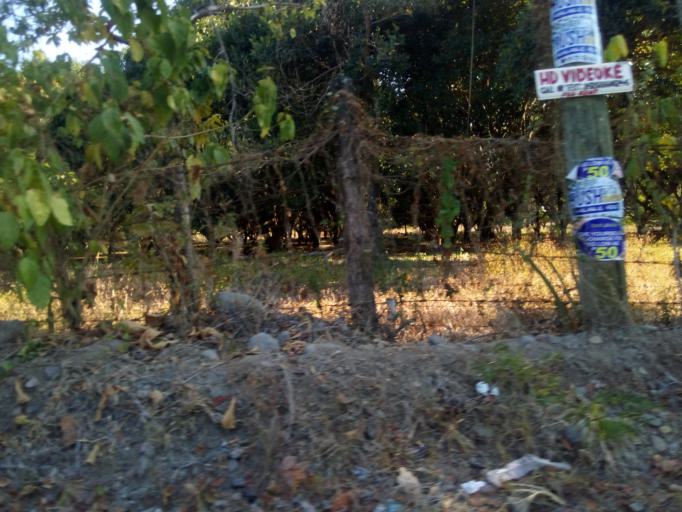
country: PH
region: Central Visayas
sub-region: Province of Negros Oriental
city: Valencia
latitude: 9.3133
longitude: 123.2603
